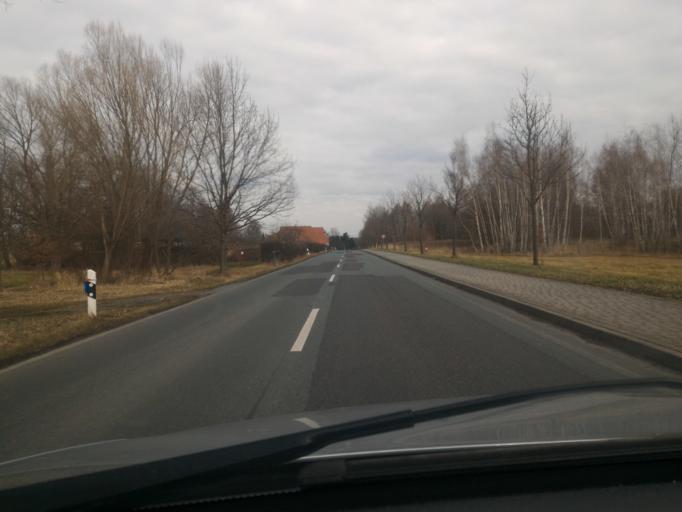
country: DE
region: Saxony
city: Zittau
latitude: 50.8682
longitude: 14.8060
